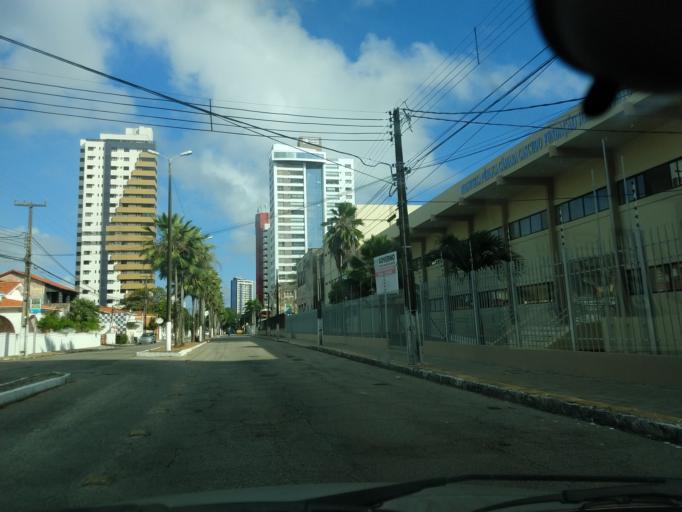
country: BR
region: Rio Grande do Norte
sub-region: Natal
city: Natal
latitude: -5.7851
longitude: -35.1973
